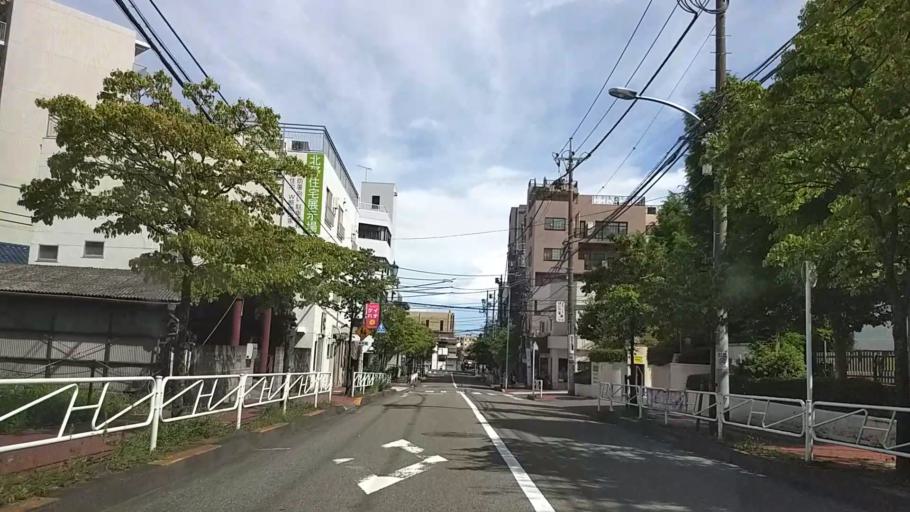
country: JP
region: Tokyo
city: Hachioji
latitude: 35.6567
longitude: 139.3434
